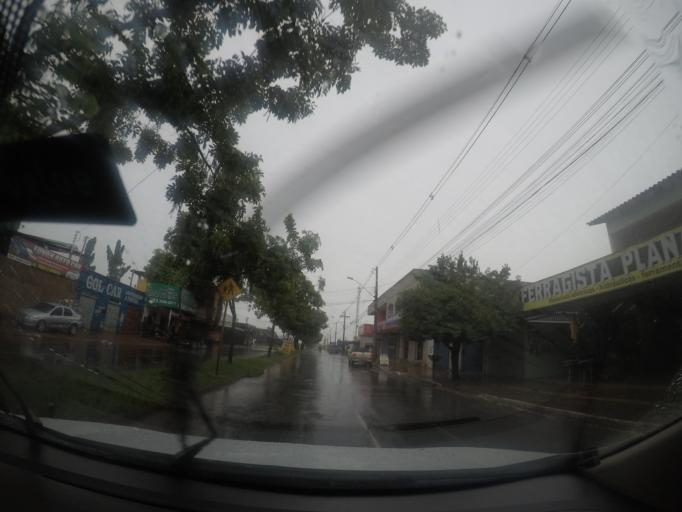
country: BR
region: Goias
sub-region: Goiania
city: Goiania
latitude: -16.6215
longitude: -49.3376
